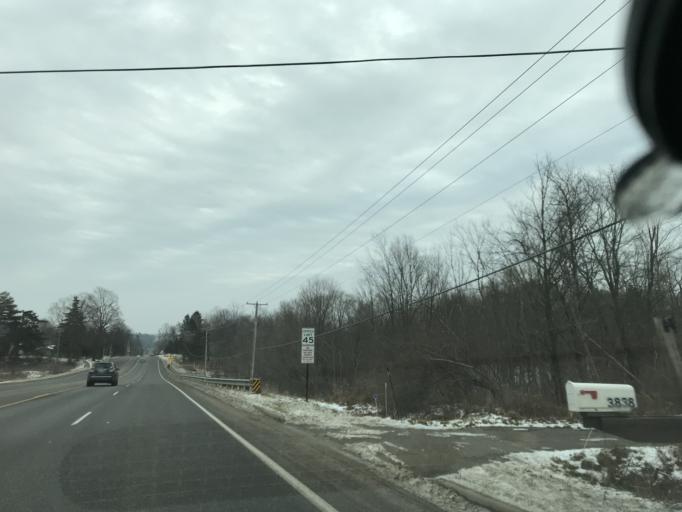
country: US
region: Michigan
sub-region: Kent County
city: Rockford
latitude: 43.1172
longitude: -85.5756
